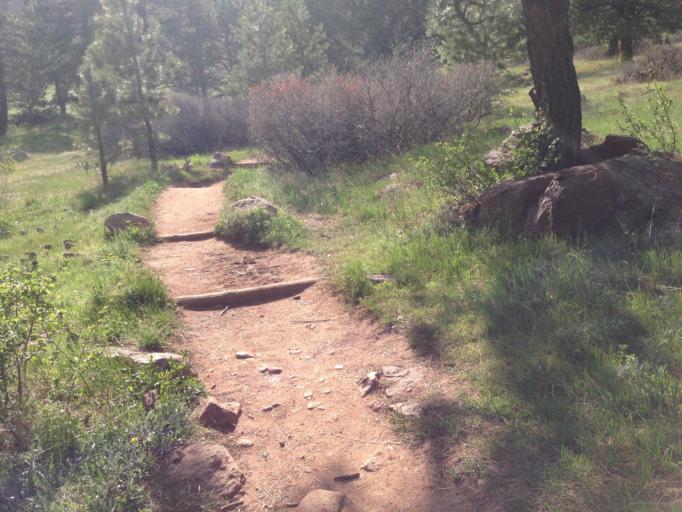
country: US
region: Colorado
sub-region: Boulder County
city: Boulder
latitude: 39.9418
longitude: -105.2705
